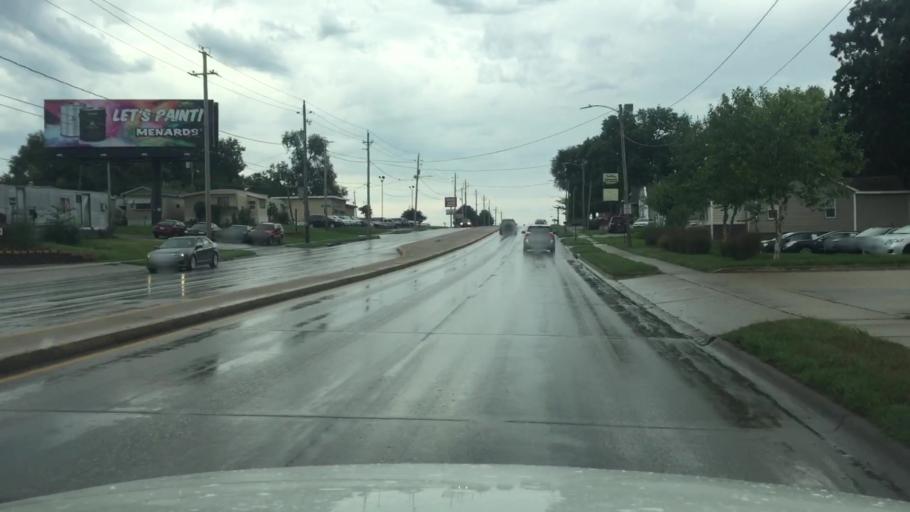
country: US
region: Iowa
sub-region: Polk County
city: Des Moines
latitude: 41.5598
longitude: -93.5970
